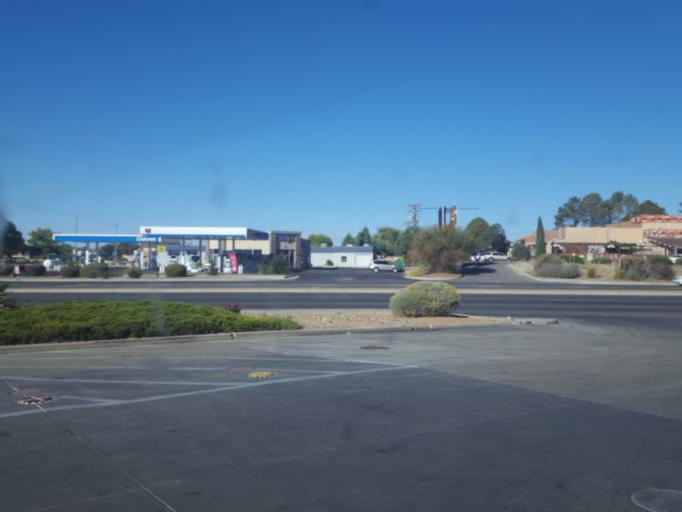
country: US
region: New Mexico
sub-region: Sandoval County
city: Rio Rancho
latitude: 35.2318
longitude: -106.6580
